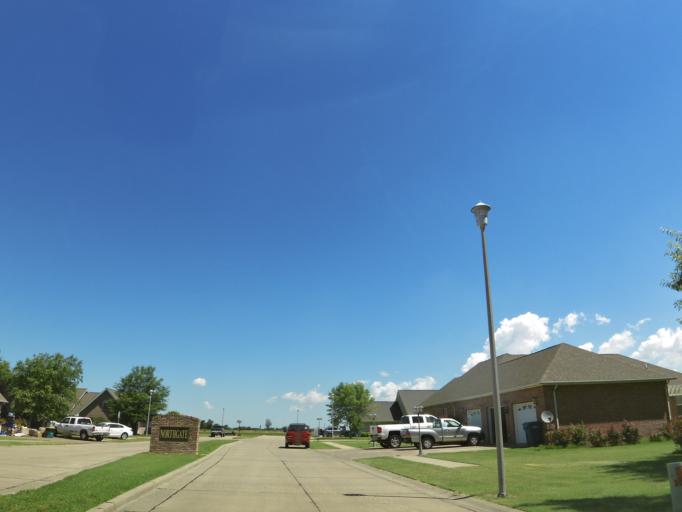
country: US
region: Missouri
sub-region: New Madrid County
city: New Madrid
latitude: 36.5988
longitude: -89.5266
